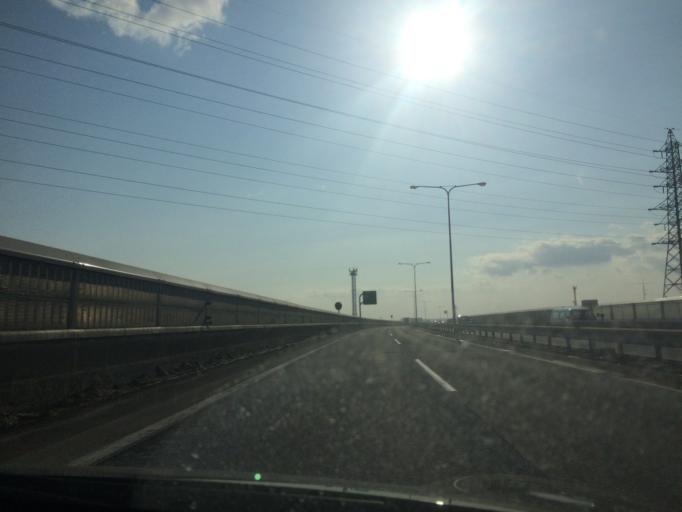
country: JP
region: Hokkaido
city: Sapporo
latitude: 43.0906
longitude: 141.4101
